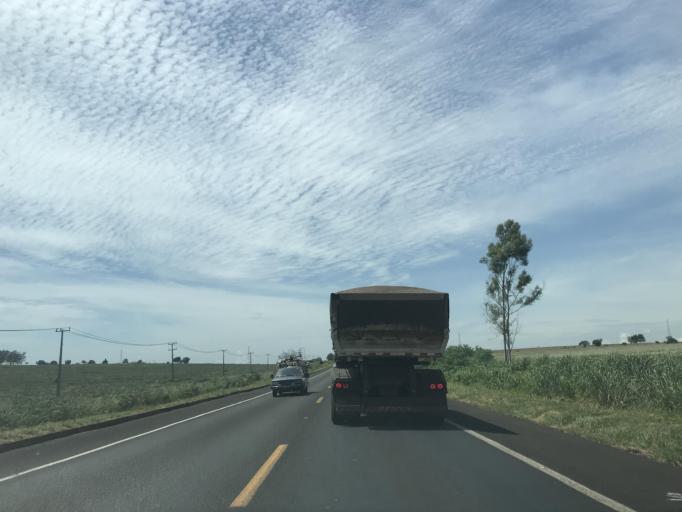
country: BR
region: Parana
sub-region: Paranavai
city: Paranavai
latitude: -23.0088
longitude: -52.5419
